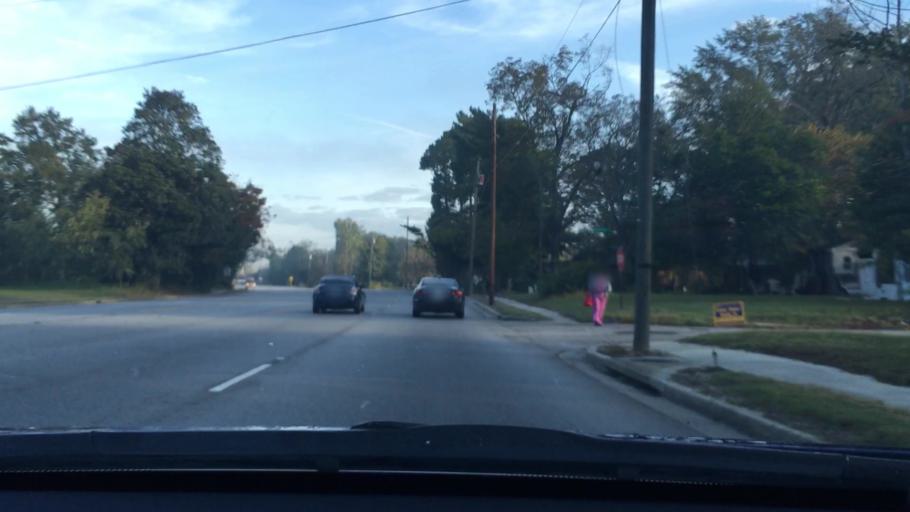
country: US
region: South Carolina
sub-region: Sumter County
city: South Sumter
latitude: 33.9036
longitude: -80.3369
